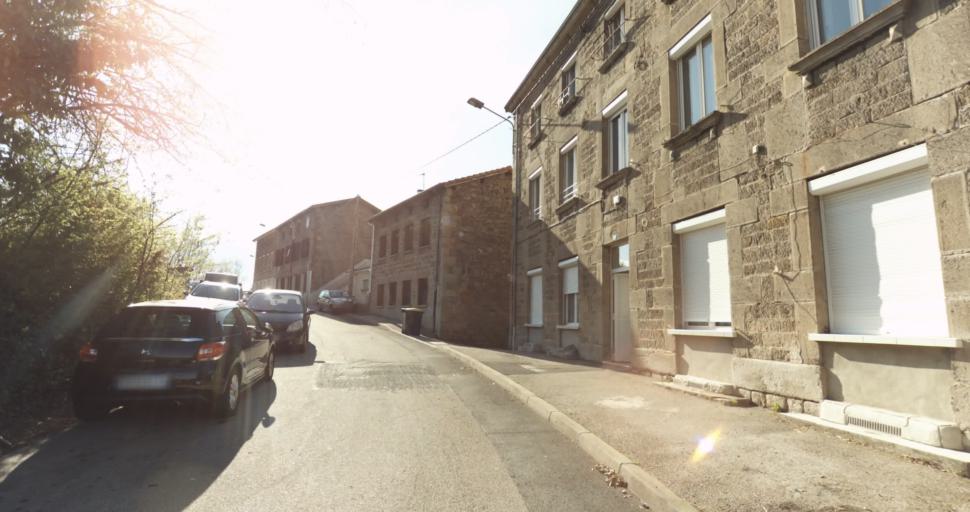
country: FR
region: Rhone-Alpes
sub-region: Departement de la Loire
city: La Talaudiere
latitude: 45.4692
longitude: 4.4377
